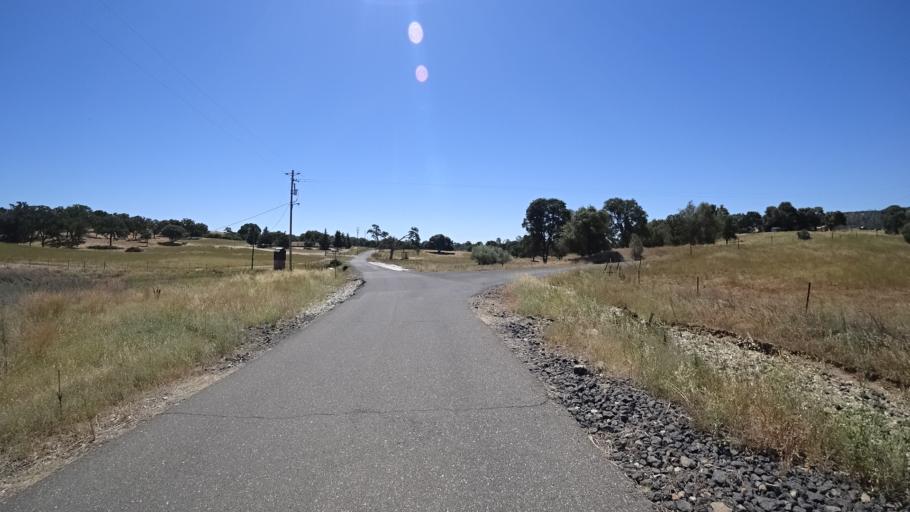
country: US
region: California
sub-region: Calaveras County
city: Copperopolis
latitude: 37.9518
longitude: -120.6845
